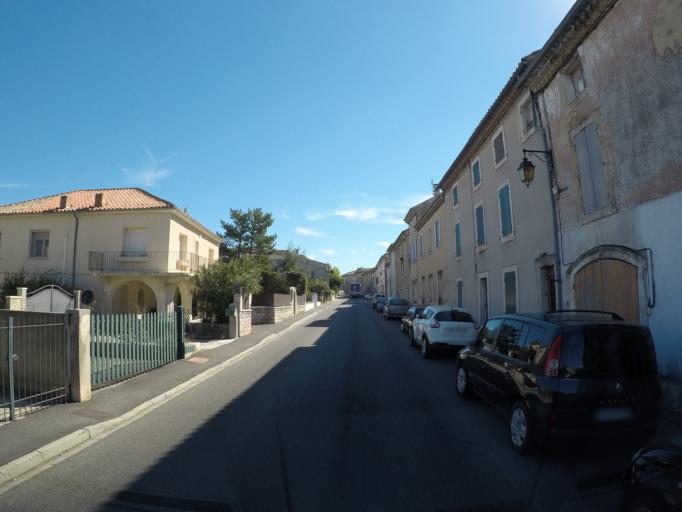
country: FR
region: Rhone-Alpes
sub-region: Departement de la Drome
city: Suze-la-Rousse
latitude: 44.2888
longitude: 4.8412
